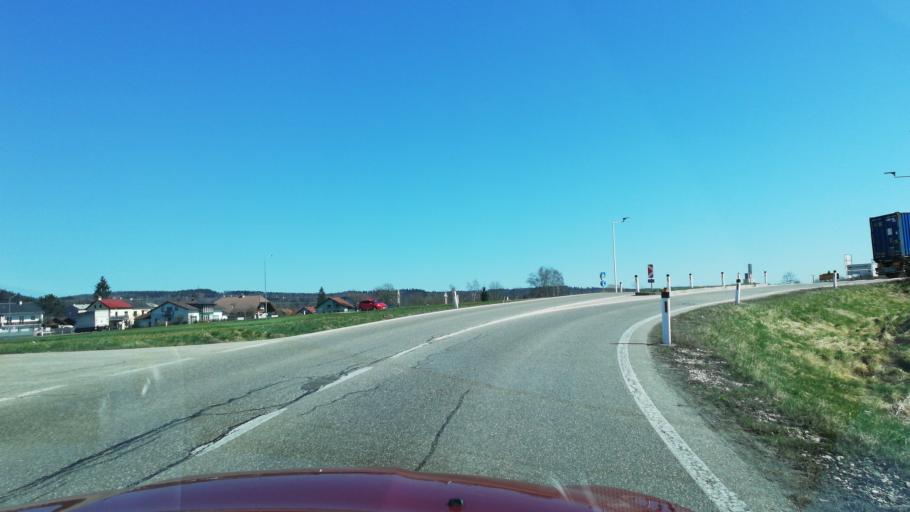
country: AT
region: Upper Austria
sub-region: Politischer Bezirk Vocklabruck
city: Timelkam
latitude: 47.9960
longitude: 13.6135
